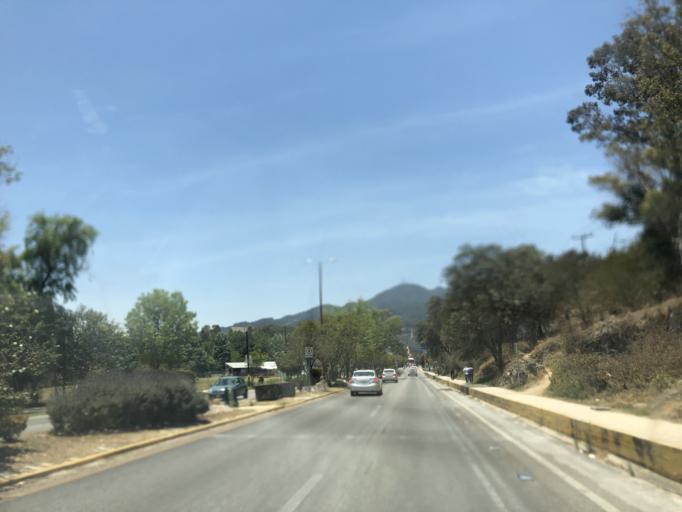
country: MX
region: Chiapas
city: San Cristobal de las Casas
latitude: 16.7317
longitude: -92.6473
